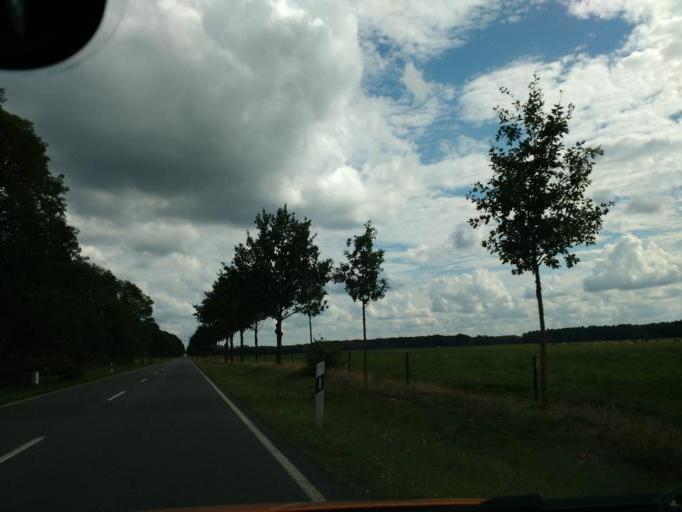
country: DE
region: Brandenburg
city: Marienwerder
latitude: 52.8563
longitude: 13.5533
